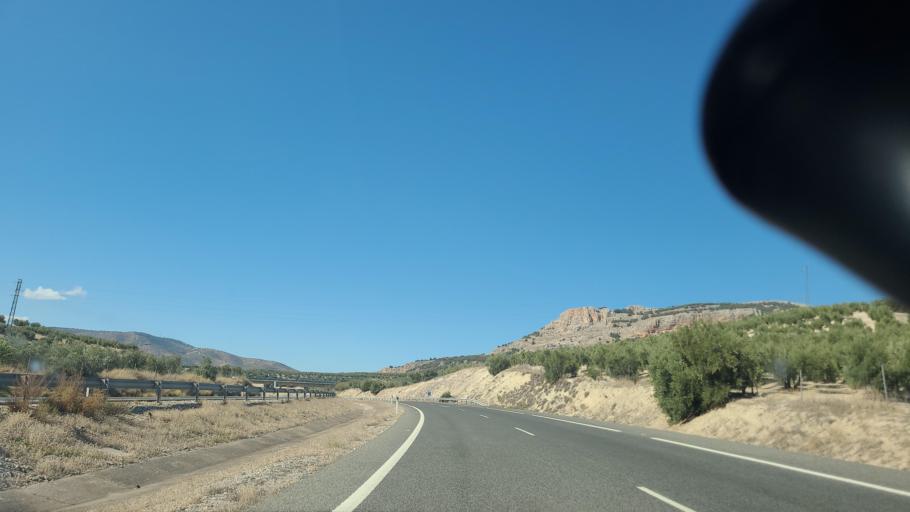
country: ES
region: Andalusia
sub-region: Provincia de Jaen
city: Pegalajar
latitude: 37.7175
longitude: -3.6487
